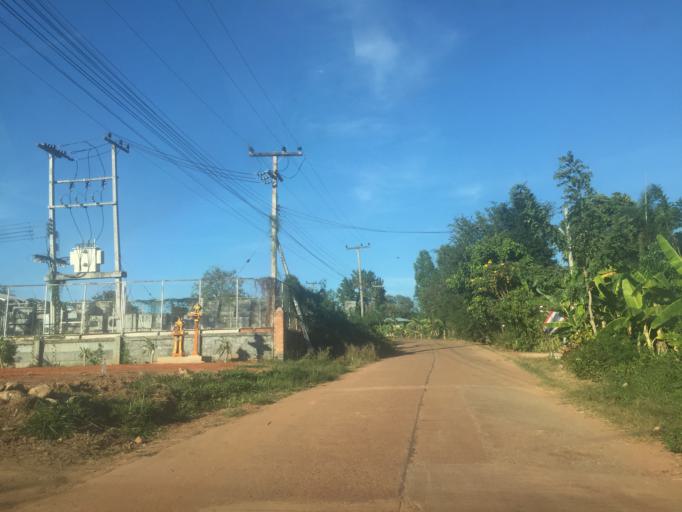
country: TH
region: Changwat Udon Thani
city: Si That
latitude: 16.9703
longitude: 103.2320
